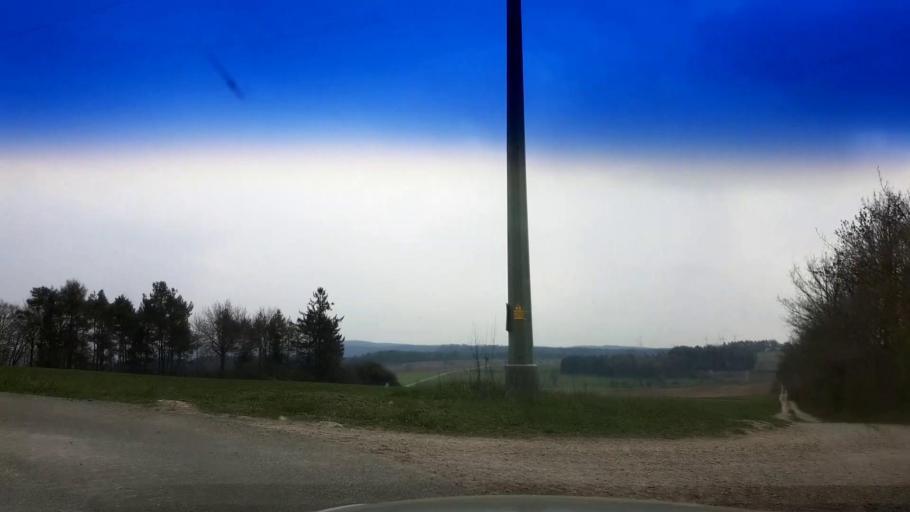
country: DE
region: Bavaria
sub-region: Upper Franconia
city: Poxdorf
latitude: 49.9061
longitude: 11.0870
